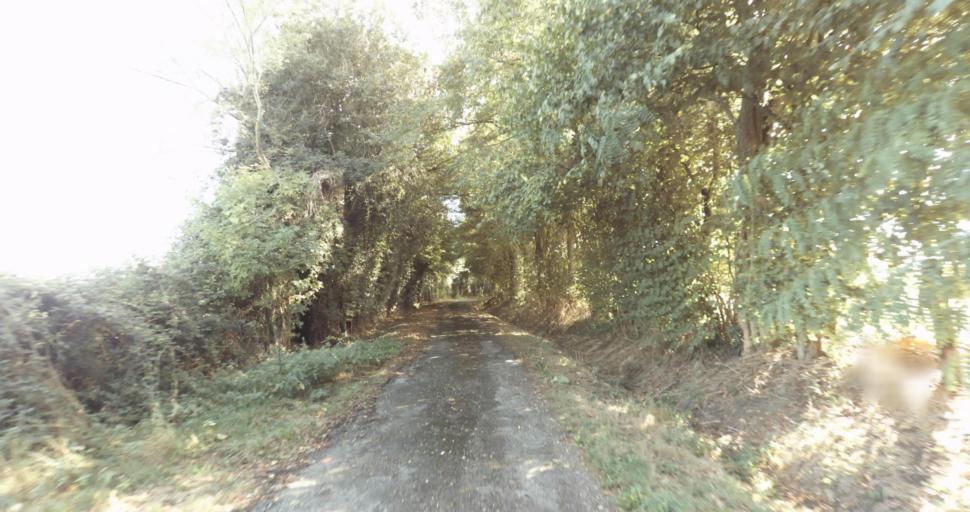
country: FR
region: Lower Normandy
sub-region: Departement de l'Orne
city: Vimoutiers
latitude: 48.9327
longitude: 0.1350
